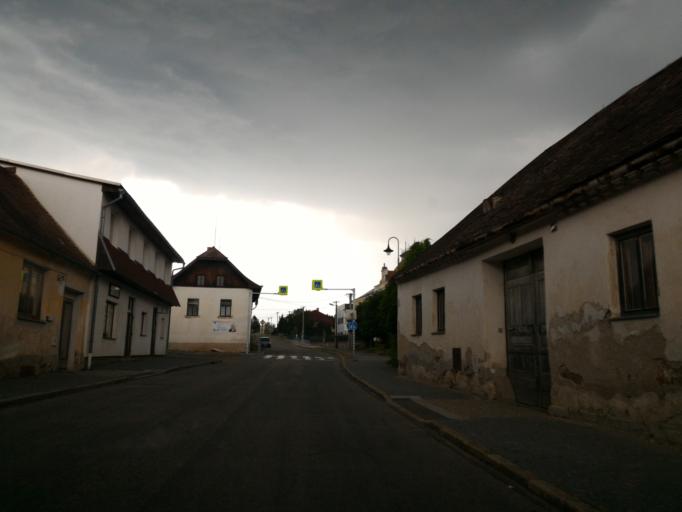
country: CZ
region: Vysocina
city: Zeletava
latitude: 49.1412
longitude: 15.5597
